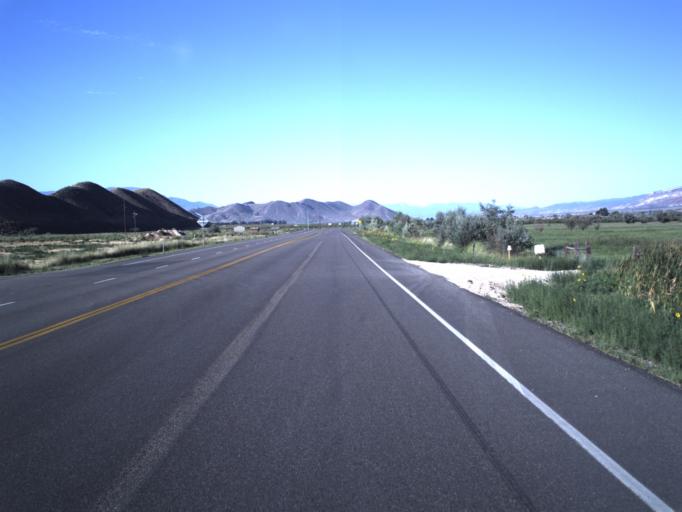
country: US
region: Utah
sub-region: Sevier County
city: Salina
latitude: 38.9469
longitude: -111.8807
